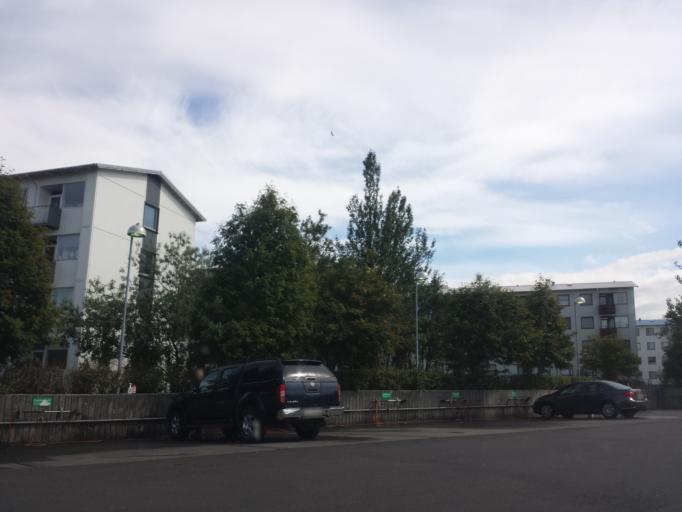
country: IS
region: Capital Region
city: Reykjavik
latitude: 64.1323
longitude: -21.8665
